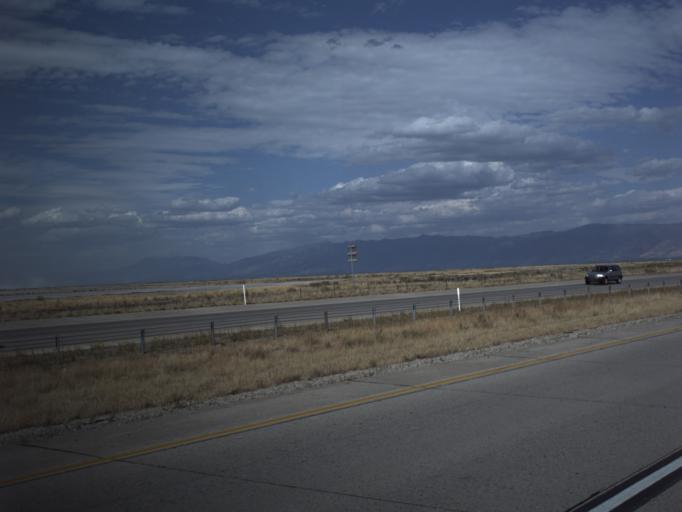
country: US
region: Utah
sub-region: Salt Lake County
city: Magna
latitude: 40.7703
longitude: -112.1503
